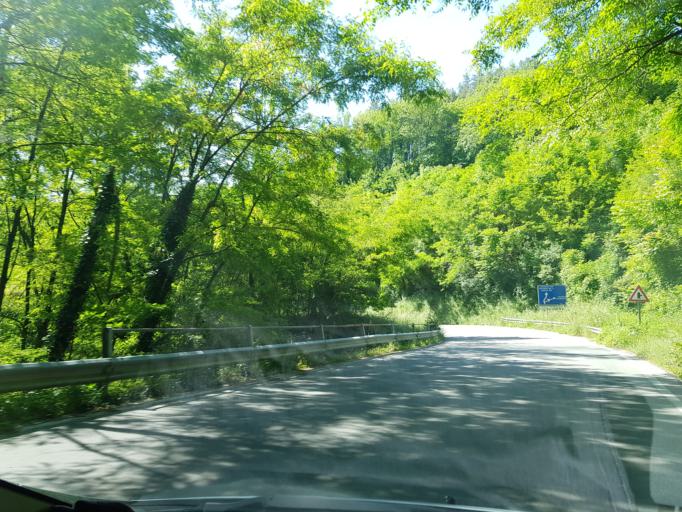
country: IT
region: Tuscany
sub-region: Provincia di Lucca
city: Camporgiano
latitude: 44.1707
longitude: 10.3160
